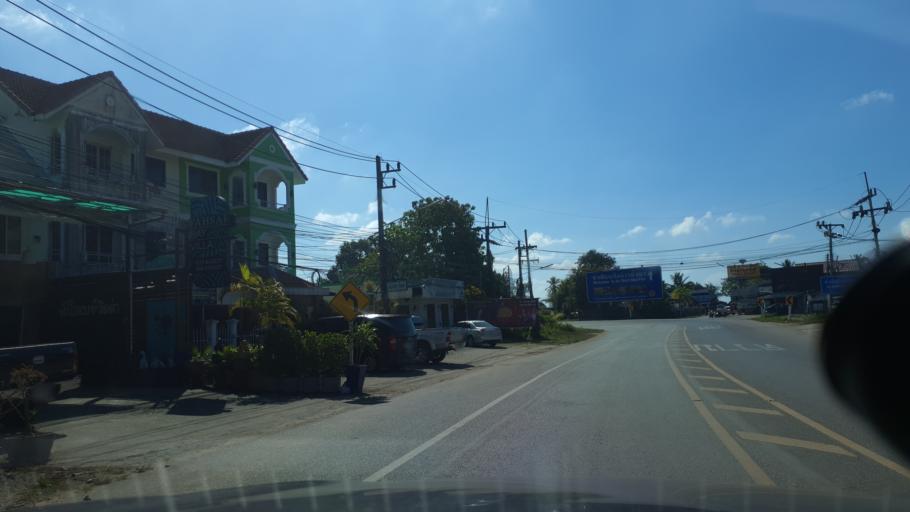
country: TH
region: Phangnga
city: Ban Ao Nang
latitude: 8.0314
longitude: 98.8626
